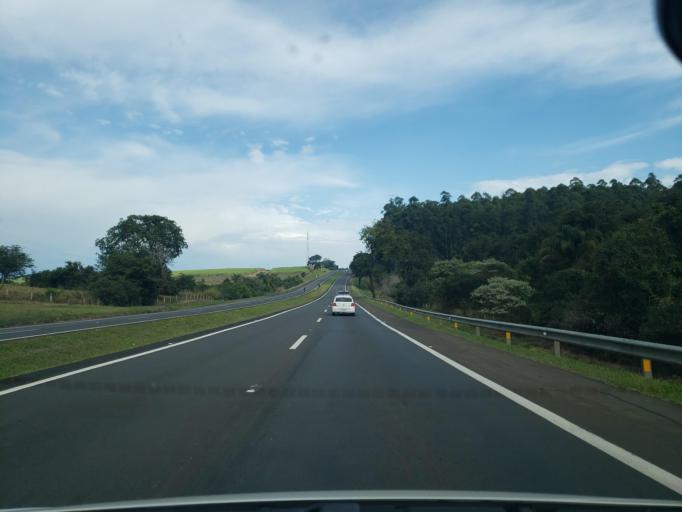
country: BR
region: Sao Paulo
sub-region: Itirapina
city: Itirapina
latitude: -22.2749
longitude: -47.9657
